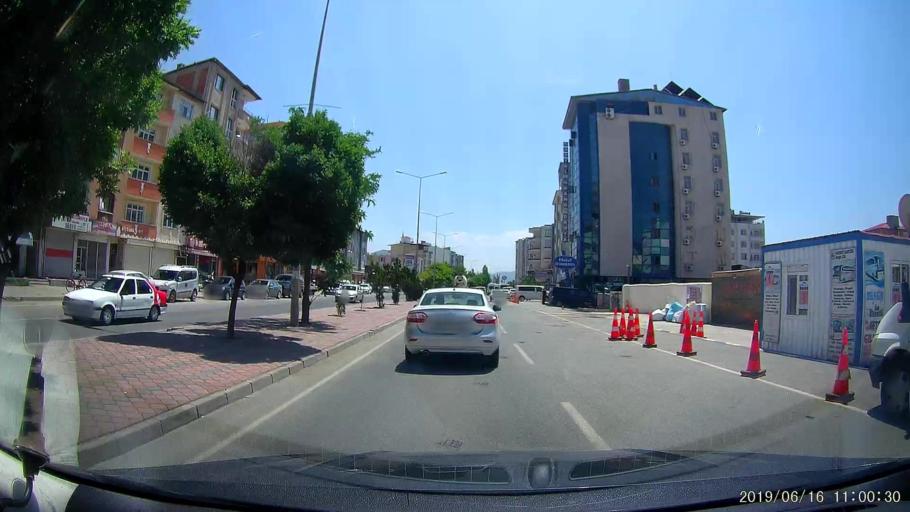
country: TR
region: Igdir
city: Igdir
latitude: 39.9183
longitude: 44.0442
